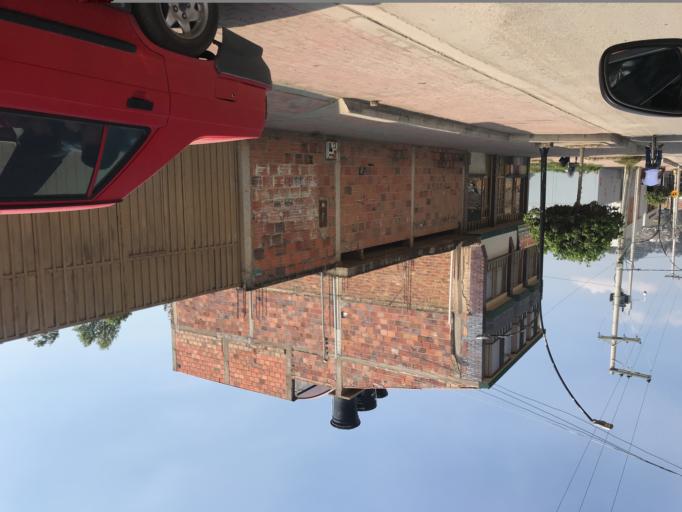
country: CO
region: Boyaca
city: Samaca
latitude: 5.4956
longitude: -73.4877
